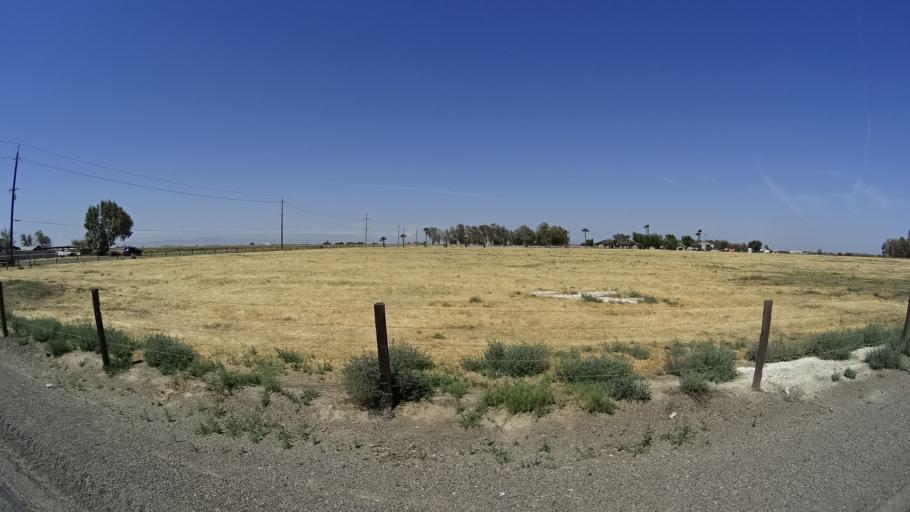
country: US
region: California
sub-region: Kings County
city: Stratford
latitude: 36.2410
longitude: -119.7985
